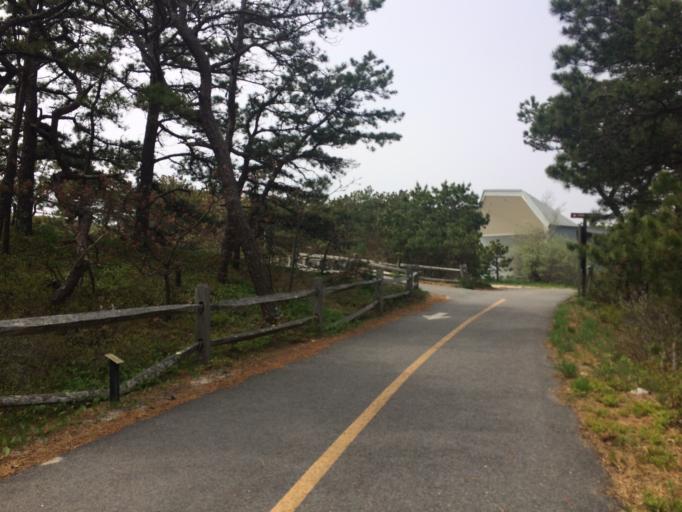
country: US
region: Massachusetts
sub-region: Barnstable County
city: Provincetown
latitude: 42.0742
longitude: -70.2061
